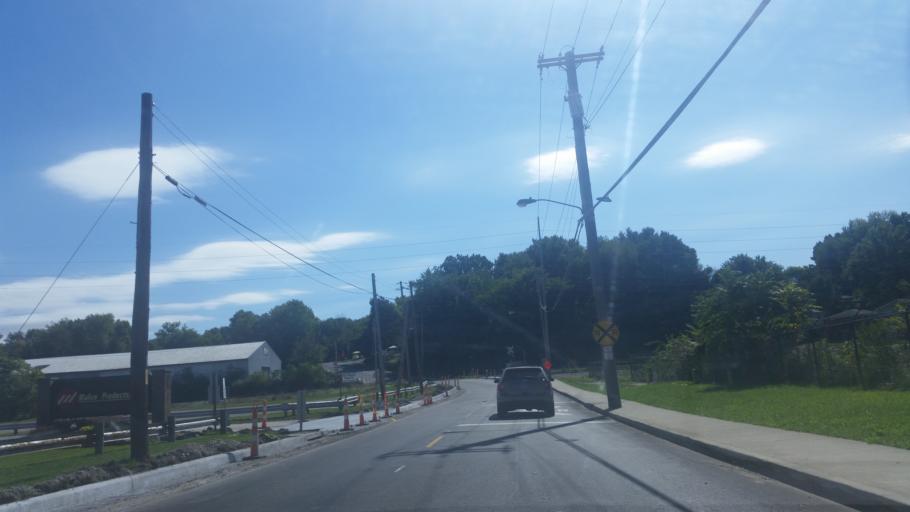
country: US
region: Ohio
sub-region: Summit County
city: Barberton
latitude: 41.0234
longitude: -81.5921
